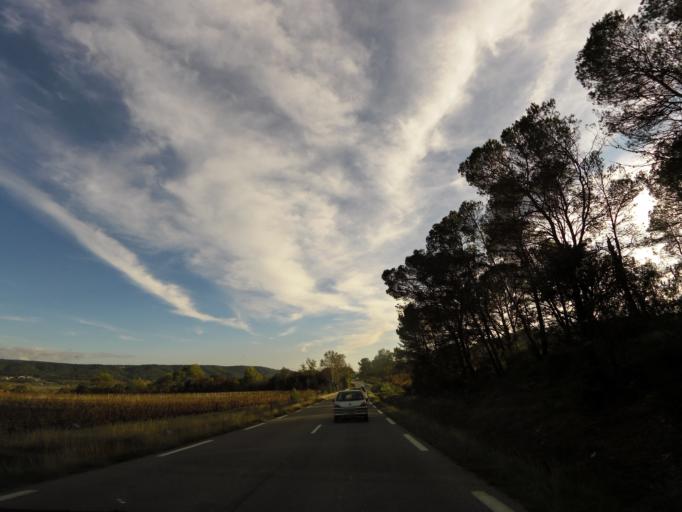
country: FR
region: Languedoc-Roussillon
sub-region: Departement du Gard
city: Ledignan
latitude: 43.9381
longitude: 4.1016
